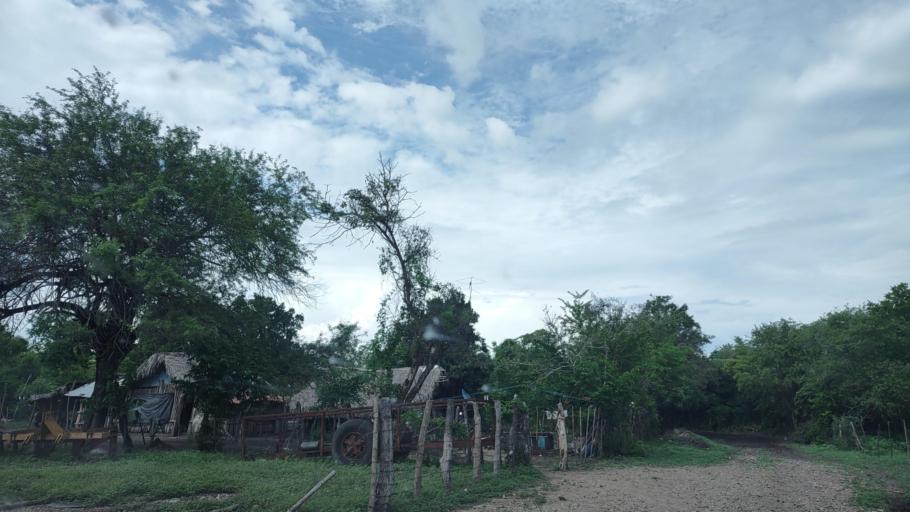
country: MX
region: Veracruz
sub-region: Panuco
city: Oviedo
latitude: 22.0024
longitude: -98.4537
